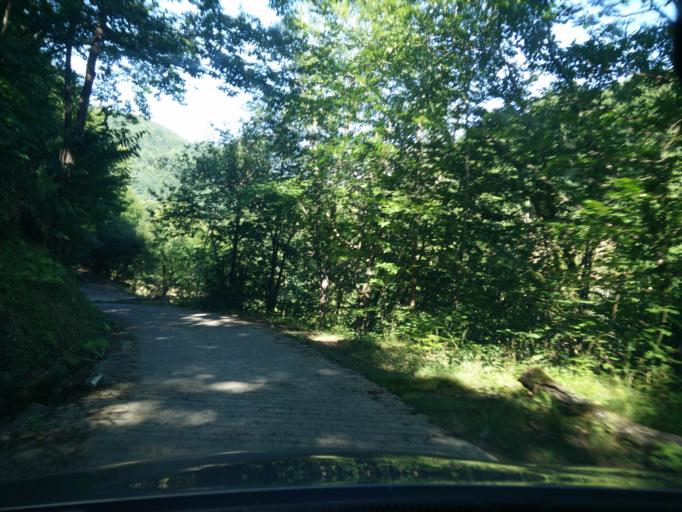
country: ES
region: Asturias
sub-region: Province of Asturias
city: Campo de Caso
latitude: 43.1499
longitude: -5.3794
